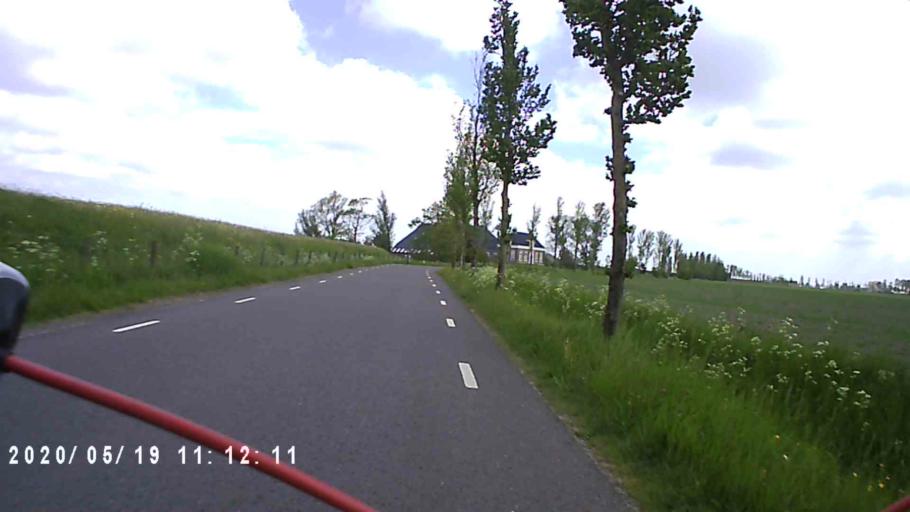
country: NL
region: Groningen
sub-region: Gemeente Zuidhorn
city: Grijpskerk
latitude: 53.2903
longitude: 6.3337
